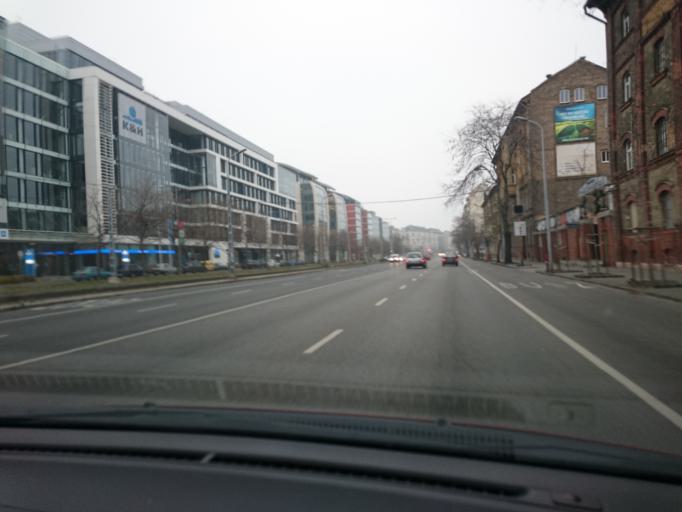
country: HU
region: Budapest
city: Budapest IX. keruelet
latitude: 47.4716
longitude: 19.0731
